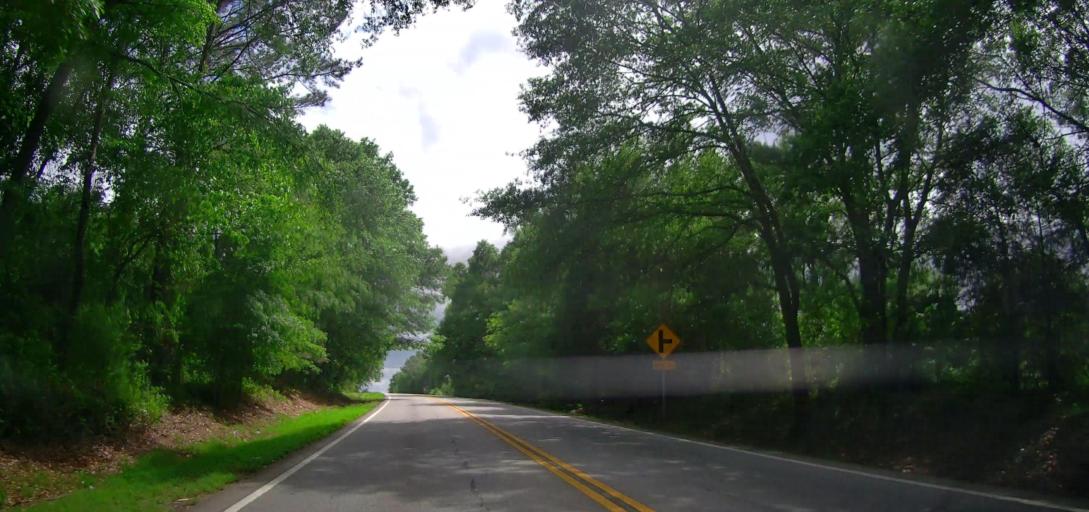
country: US
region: Georgia
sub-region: Henry County
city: Stockbridge
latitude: 33.5754
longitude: -84.1648
